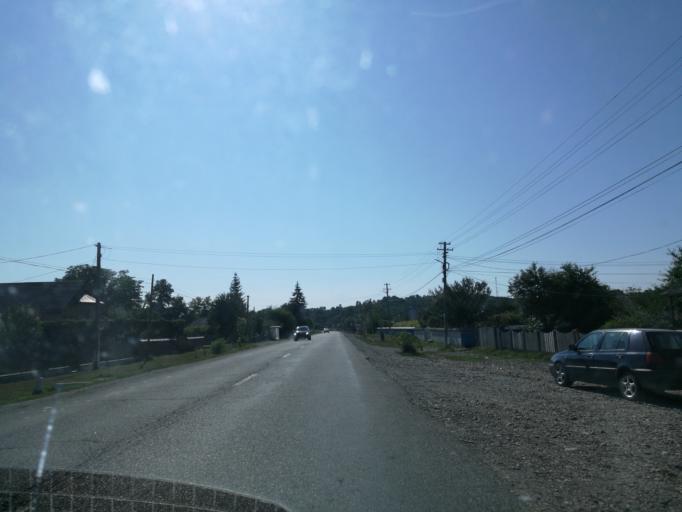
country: RO
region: Suceava
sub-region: Comuna Forasti
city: Oniceni
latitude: 47.3083
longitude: 26.4772
